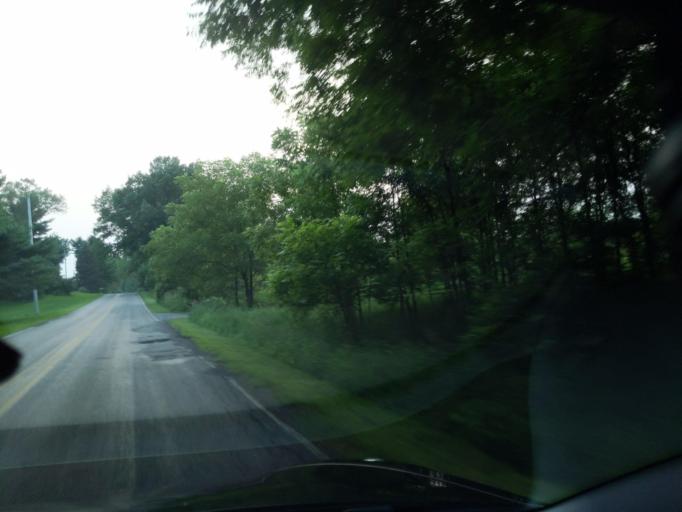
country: US
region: Michigan
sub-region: Ingham County
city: Leslie
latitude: 42.3495
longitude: -84.4681
